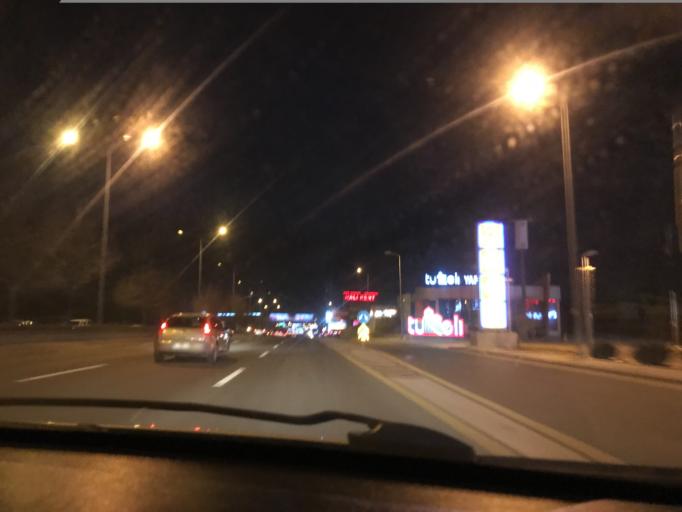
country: TR
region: Ankara
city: Batikent
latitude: 39.9454
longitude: 32.7284
